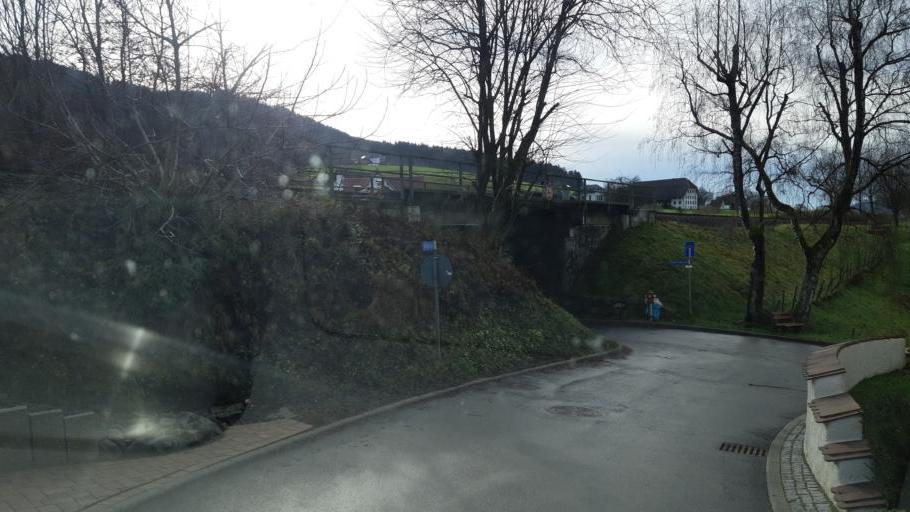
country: DE
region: Baden-Wuerttemberg
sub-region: Freiburg Region
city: Elzach
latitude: 48.1496
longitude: 8.0407
